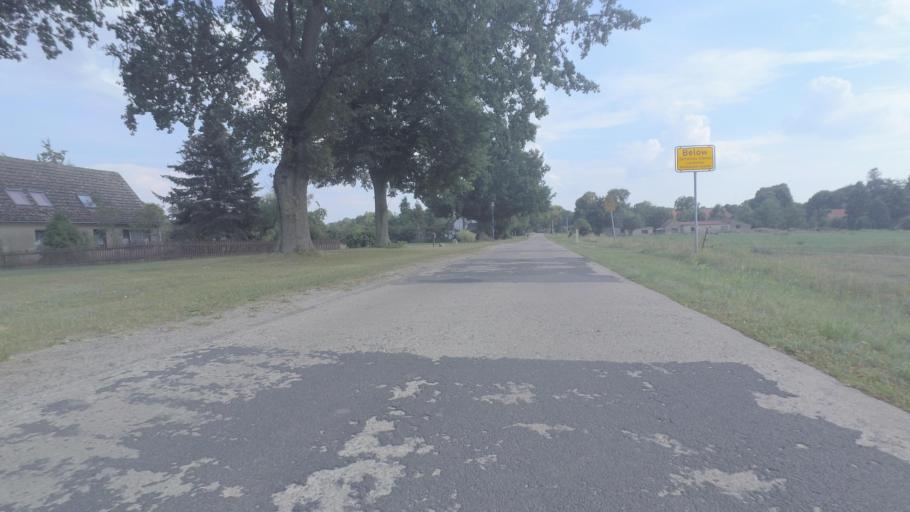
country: DE
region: Brandenburg
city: Wittstock
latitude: 53.2616
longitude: 12.4623
